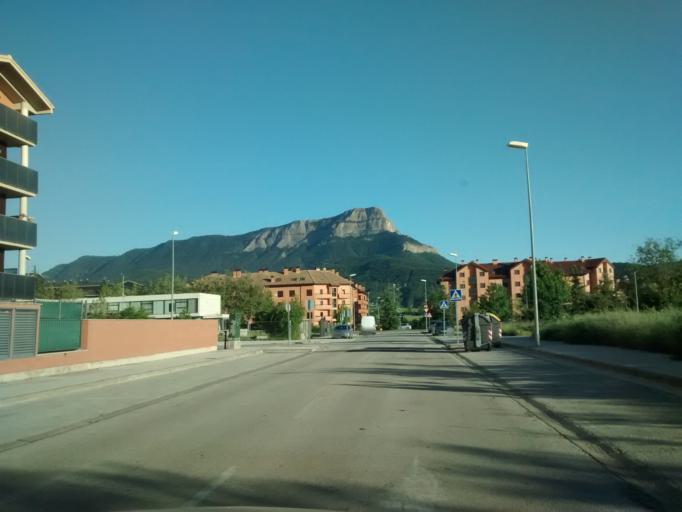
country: ES
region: Aragon
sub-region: Provincia de Huesca
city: Jaca
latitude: 42.5665
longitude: -0.5617
